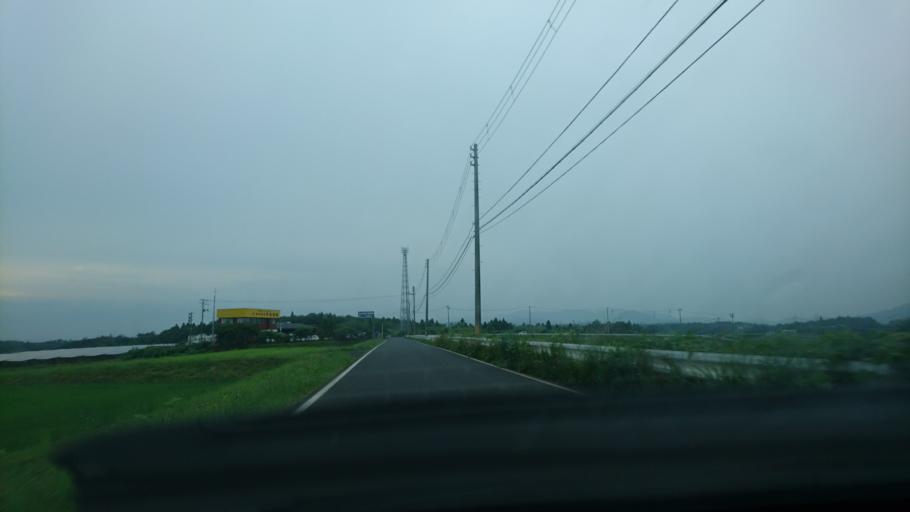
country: JP
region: Iwate
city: Ichinoseki
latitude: 38.9002
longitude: 141.1953
